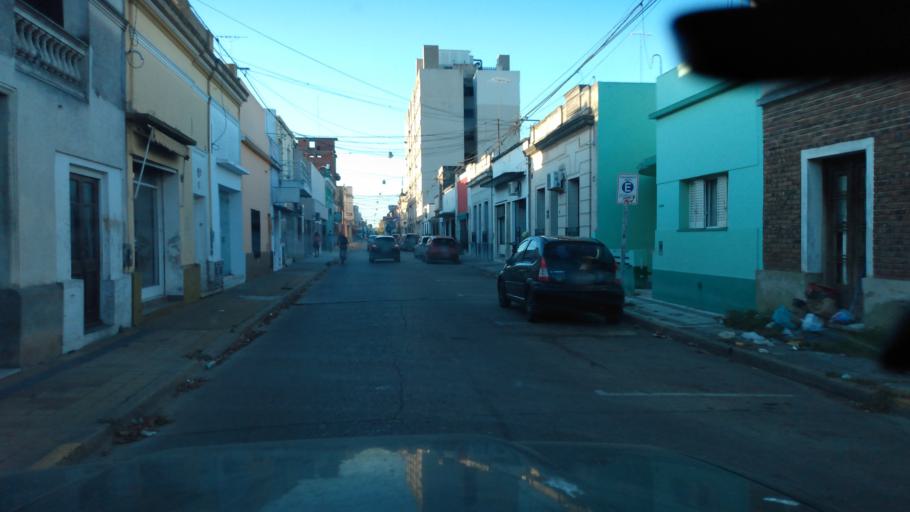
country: AR
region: Buenos Aires
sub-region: Partido de Lujan
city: Lujan
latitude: -34.5671
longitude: -59.1189
